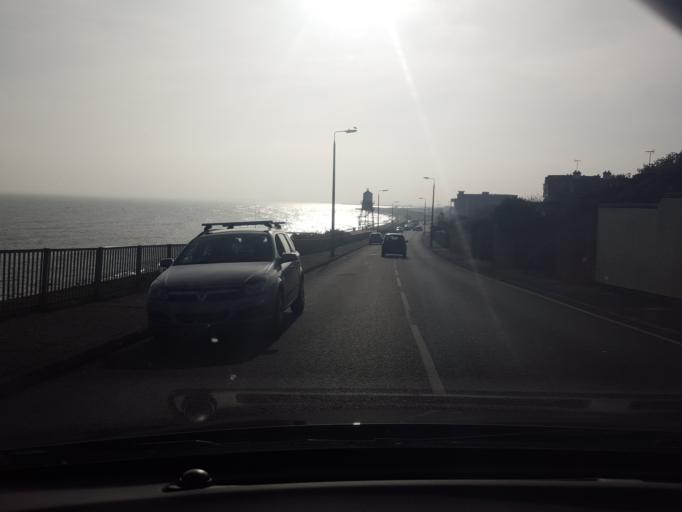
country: GB
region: England
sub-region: Essex
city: Dovercourt
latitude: 51.9325
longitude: 1.2773
